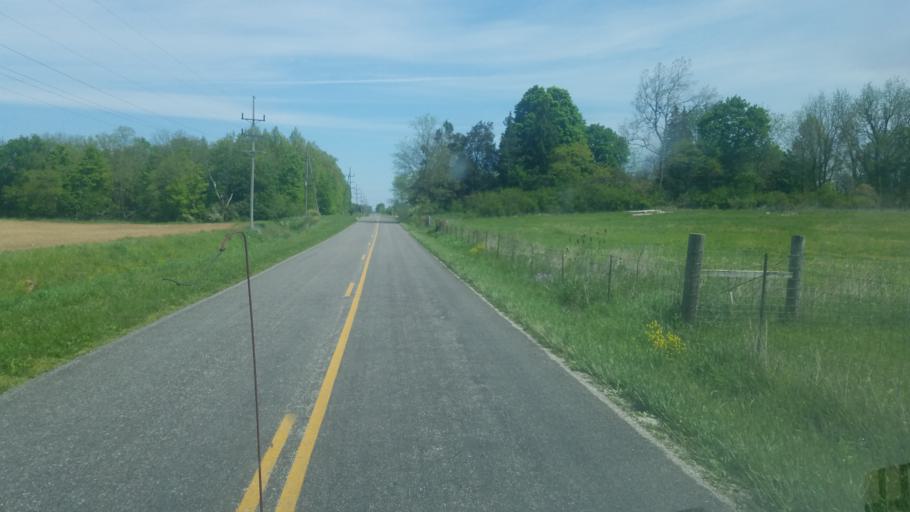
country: US
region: Ohio
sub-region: Seneca County
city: Tiffin
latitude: 41.0861
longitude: -83.1316
